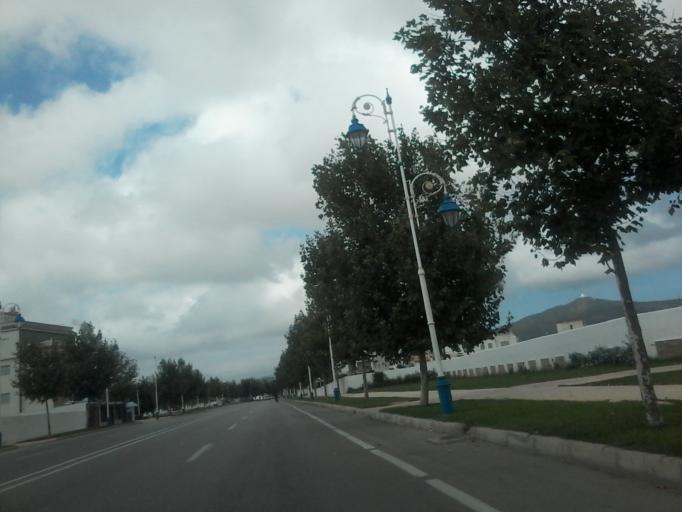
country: MA
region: Tanger-Tetouan
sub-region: Tetouan
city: Martil
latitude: 35.6398
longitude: -5.2914
